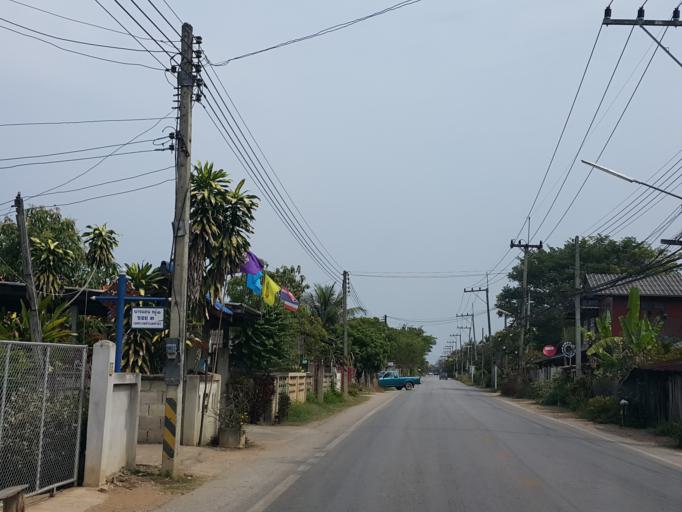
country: TH
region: Lampang
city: Ko Kha
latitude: 18.1654
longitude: 99.3836
